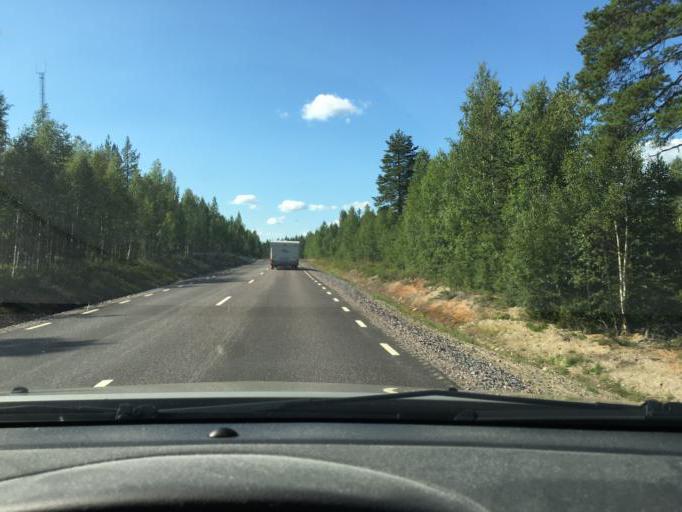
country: SE
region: Norrbotten
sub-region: Lulea Kommun
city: Ranea
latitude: 66.0507
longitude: 22.2260
